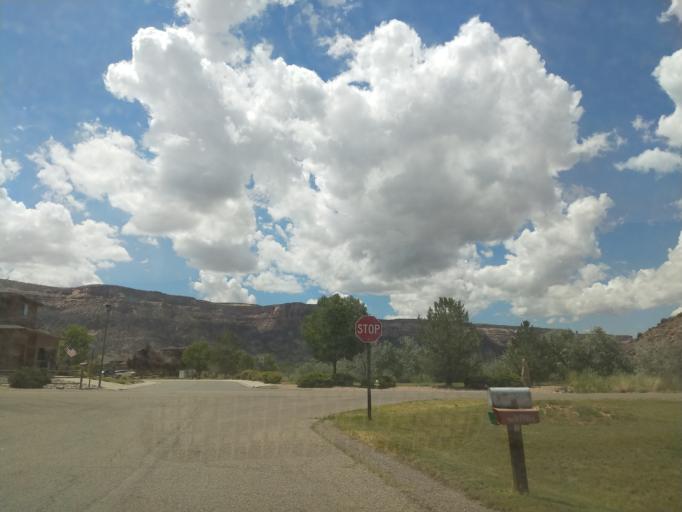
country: US
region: Colorado
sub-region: Mesa County
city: Redlands
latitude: 39.0720
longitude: -108.6488
